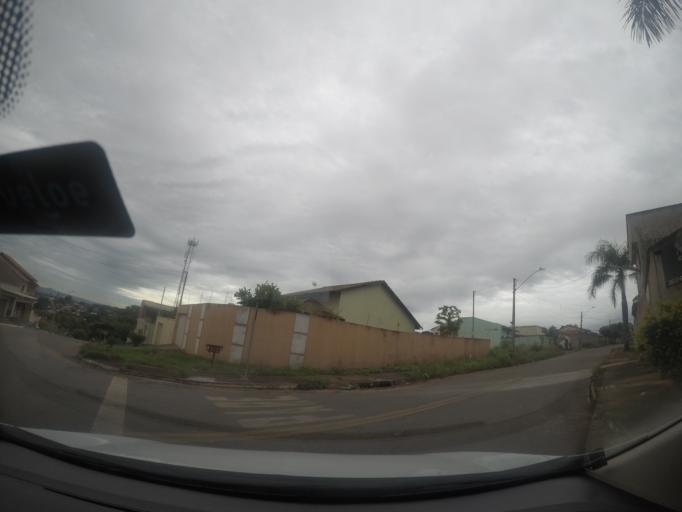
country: BR
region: Goias
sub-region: Goiania
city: Goiania
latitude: -16.6131
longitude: -49.3081
